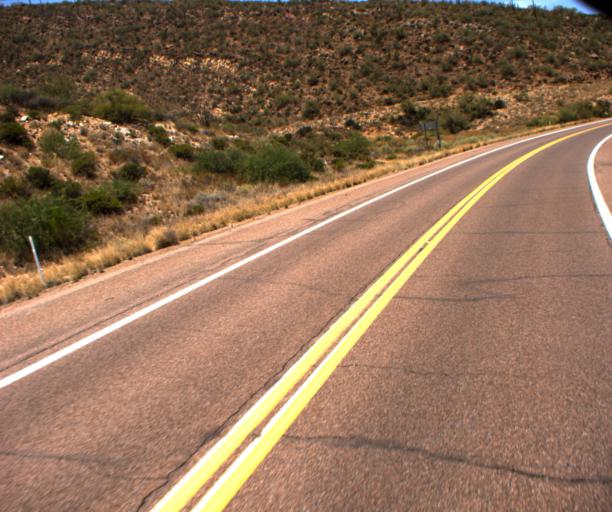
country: US
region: Arizona
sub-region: Gila County
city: Tonto Basin
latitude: 33.6893
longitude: -111.1758
